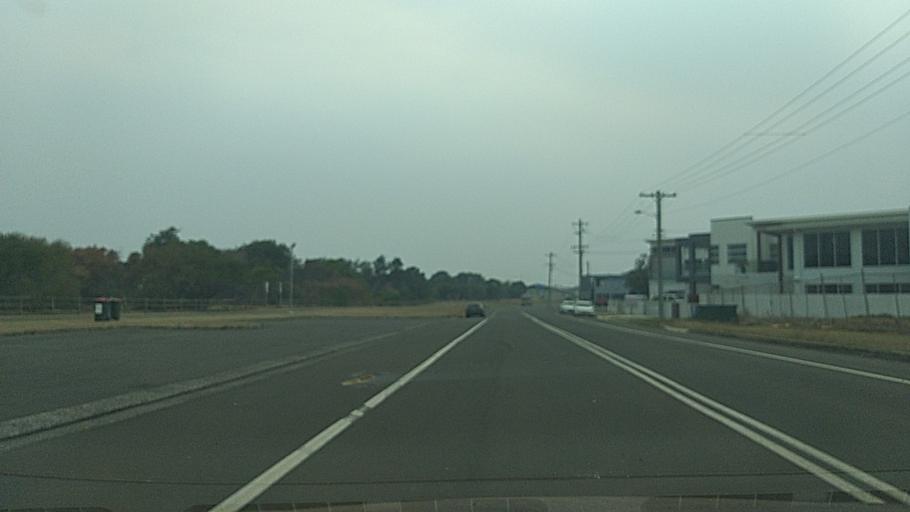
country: AU
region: New South Wales
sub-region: Shellharbour
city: Lake Illawarra
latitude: -34.5465
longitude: 150.8698
